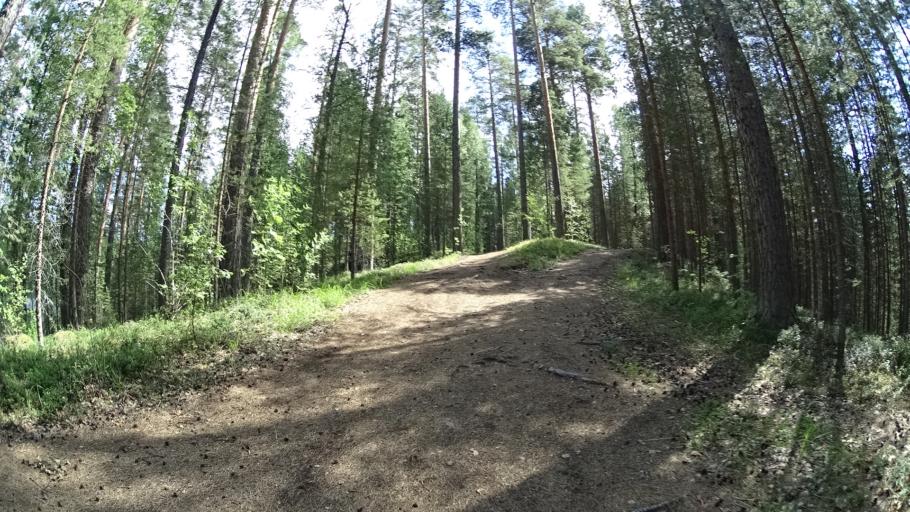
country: FI
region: Southern Savonia
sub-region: Savonlinna
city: Punkaharju
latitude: 61.7909
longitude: 29.3072
